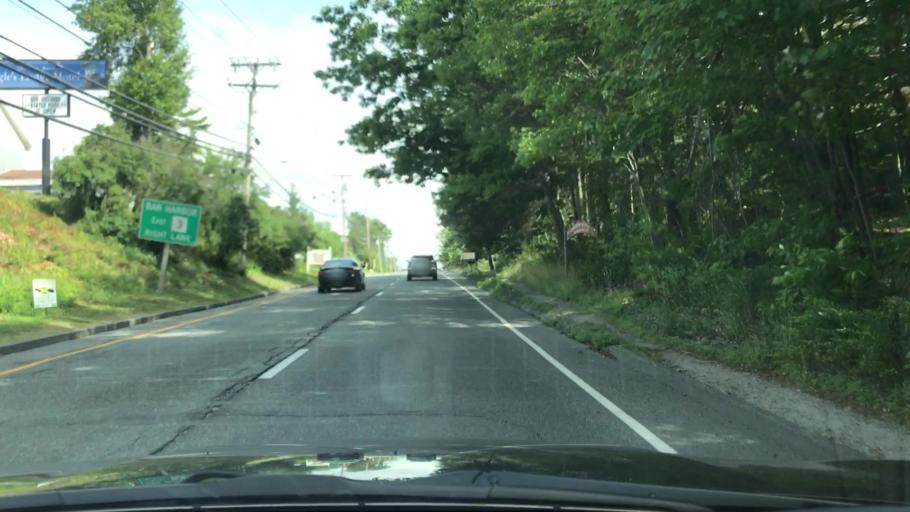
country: US
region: Maine
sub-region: Hancock County
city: Ellsworth
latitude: 44.5291
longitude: -68.4041
